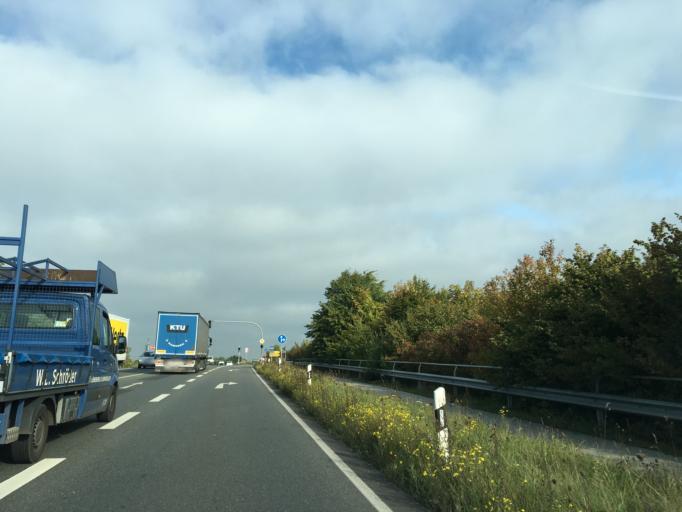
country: DE
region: Lower Saxony
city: Bardowick
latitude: 53.2762
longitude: 10.4015
